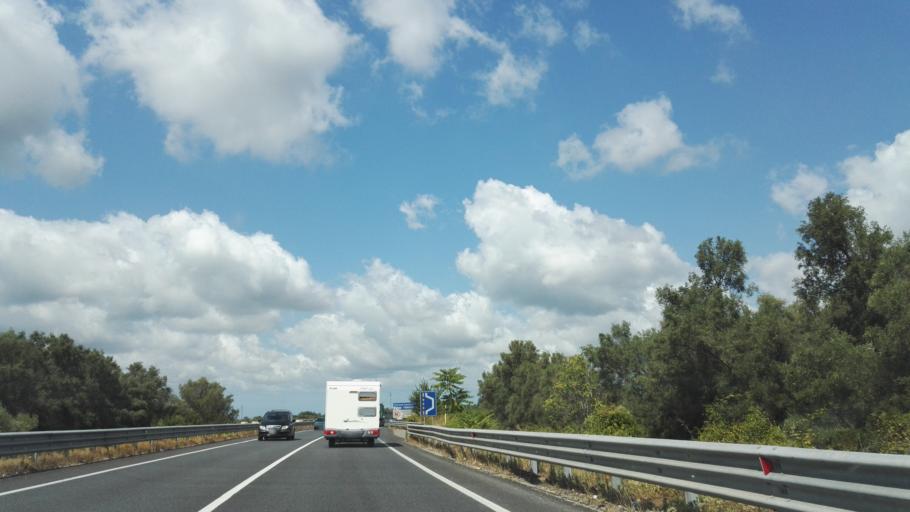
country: IT
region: Calabria
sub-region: Provincia di Reggio Calabria
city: Cinque Frondi
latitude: 38.4175
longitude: 16.0734
